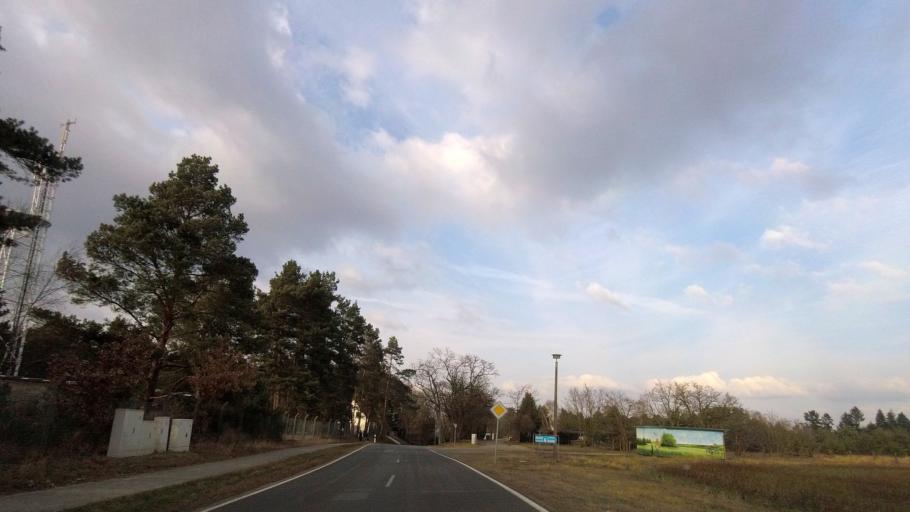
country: DE
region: Brandenburg
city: Belzig
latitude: 52.1314
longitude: 12.5862
